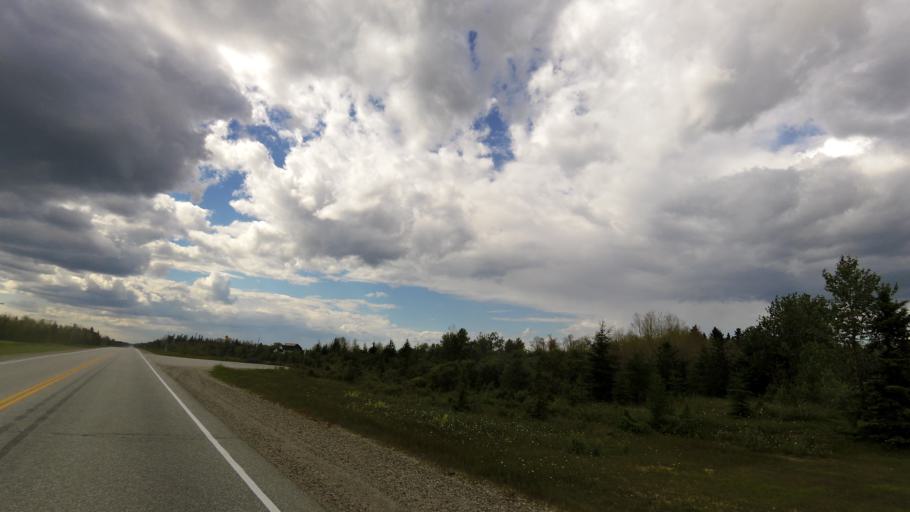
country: CA
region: Ontario
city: Hearst
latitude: 49.7136
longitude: -83.8158
